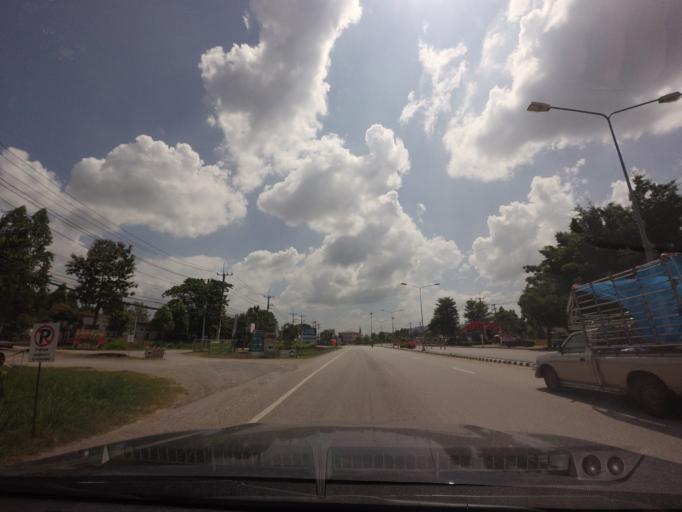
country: TH
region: Phetchabun
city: Phetchabun
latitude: 16.2639
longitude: 101.0479
